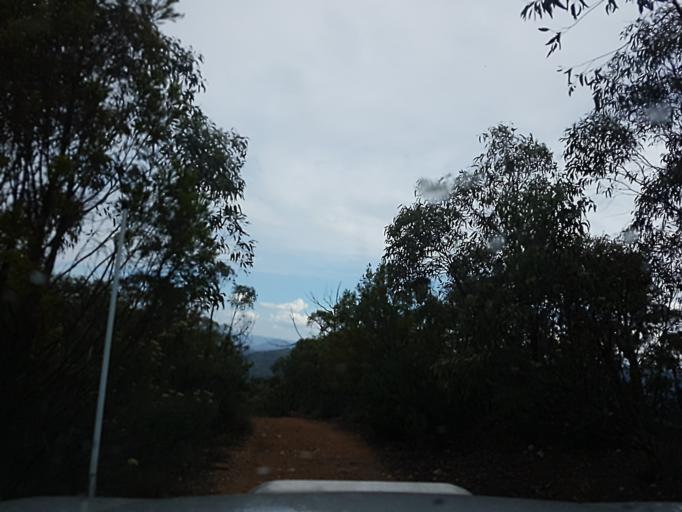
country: AU
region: New South Wales
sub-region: Snowy River
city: Jindabyne
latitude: -36.9233
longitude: 148.3415
